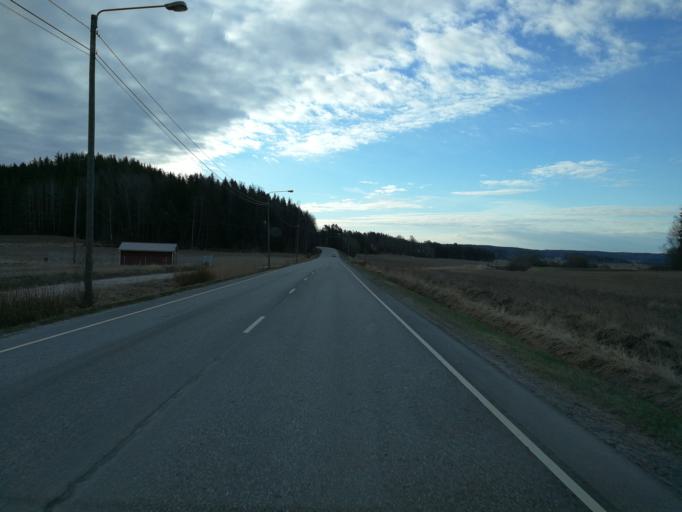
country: FI
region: Varsinais-Suomi
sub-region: Turku
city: Paimio
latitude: 60.4262
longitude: 22.6276
